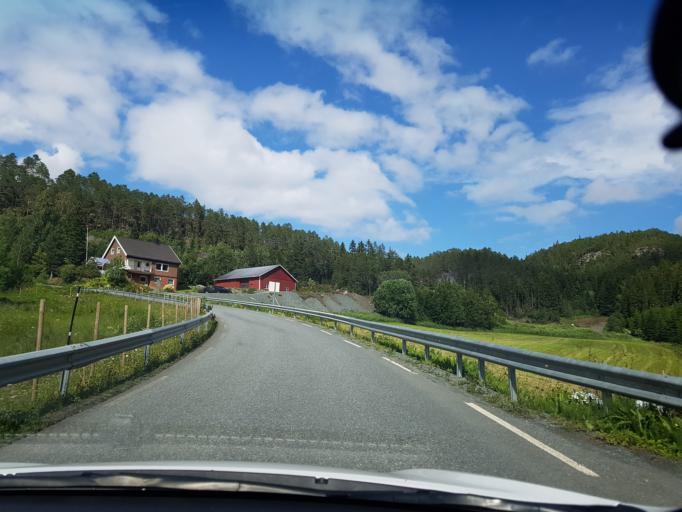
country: NO
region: Nord-Trondelag
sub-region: Frosta
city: Frosta
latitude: 63.6050
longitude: 10.8451
